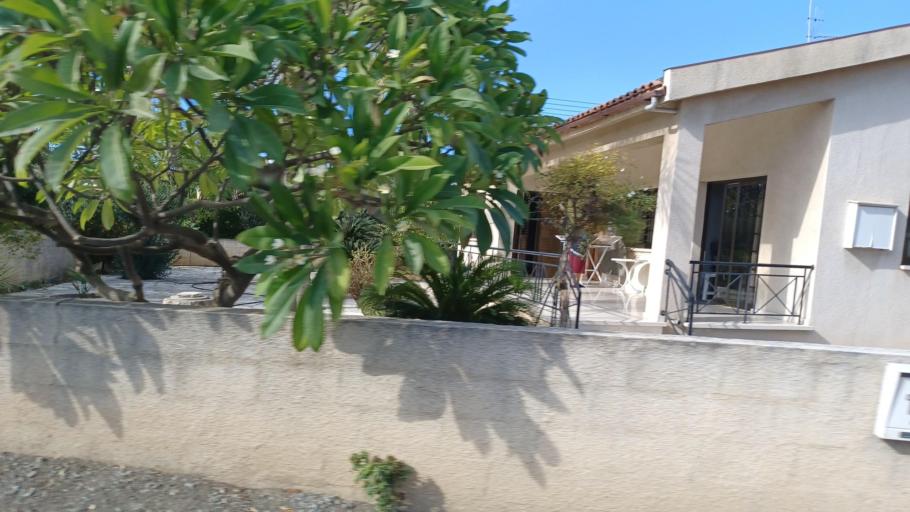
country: CY
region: Limassol
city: Pano Polemidia
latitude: 34.6976
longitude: 32.9995
